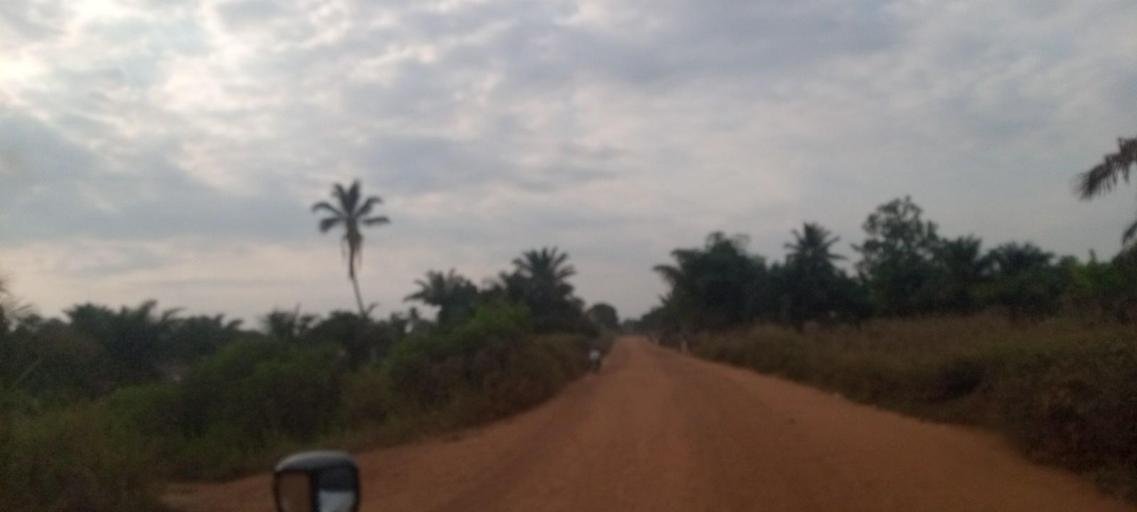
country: CD
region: Kasai-Oriental
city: Mbuji-Mayi
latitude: -6.1620
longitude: 23.7073
